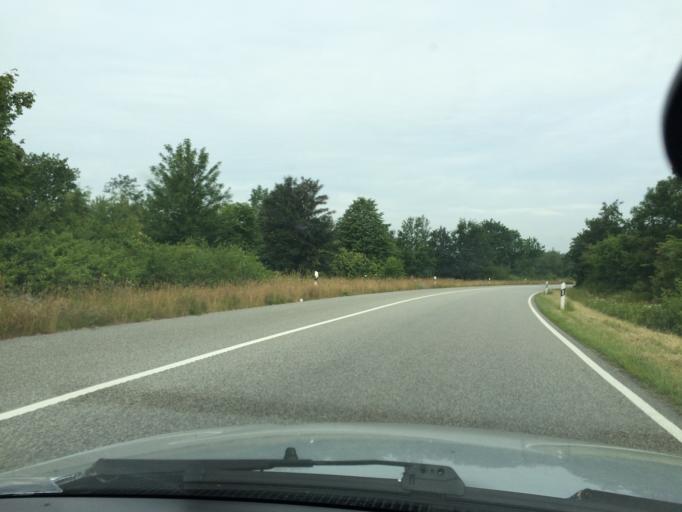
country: DE
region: Schleswig-Holstein
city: Jarplund-Weding
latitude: 54.7578
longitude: 9.4328
